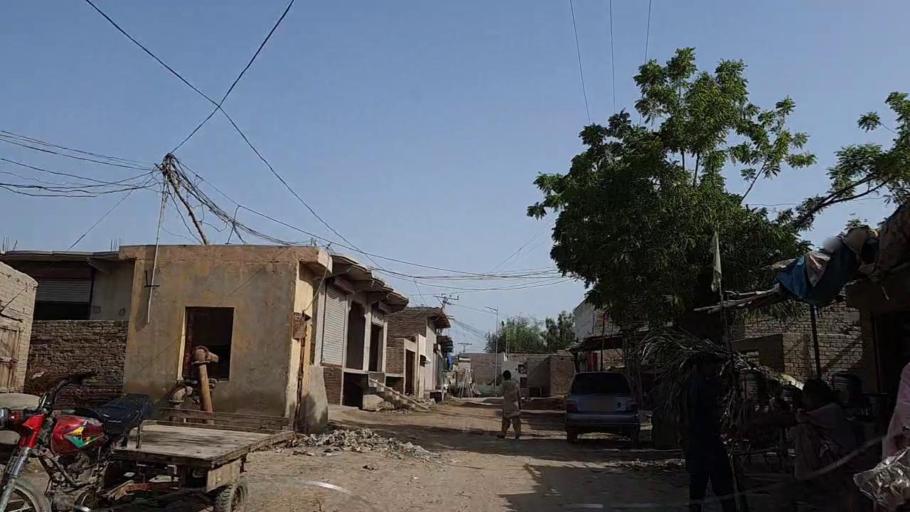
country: PK
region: Sindh
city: Kandiaro
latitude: 27.0640
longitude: 68.2066
